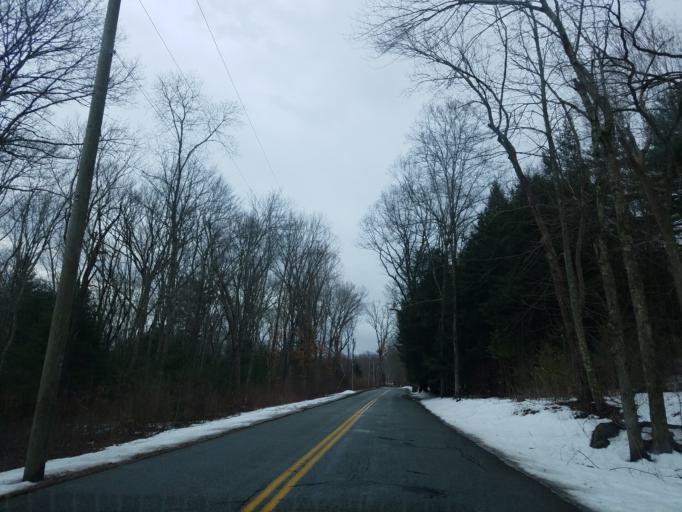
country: US
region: Connecticut
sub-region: Hartford County
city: Glastonbury Center
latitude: 41.6677
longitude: -72.5486
